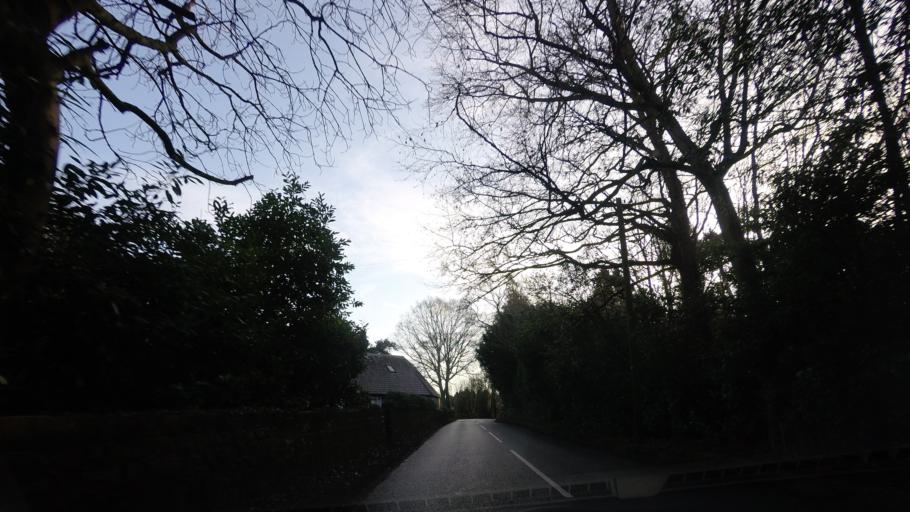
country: GB
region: England
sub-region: Kent
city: Borough Green
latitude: 51.2785
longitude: 0.2843
